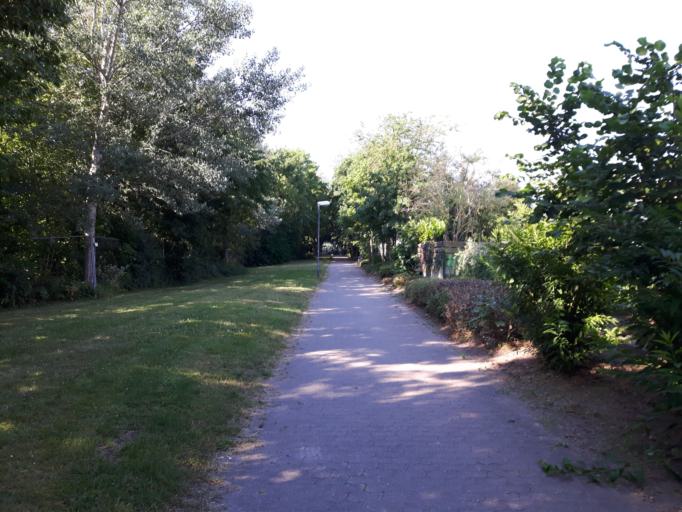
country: DE
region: Baden-Wuerttemberg
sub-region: Karlsruhe Region
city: Karlsdorf-Neuthard
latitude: 49.0979
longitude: 8.5332
